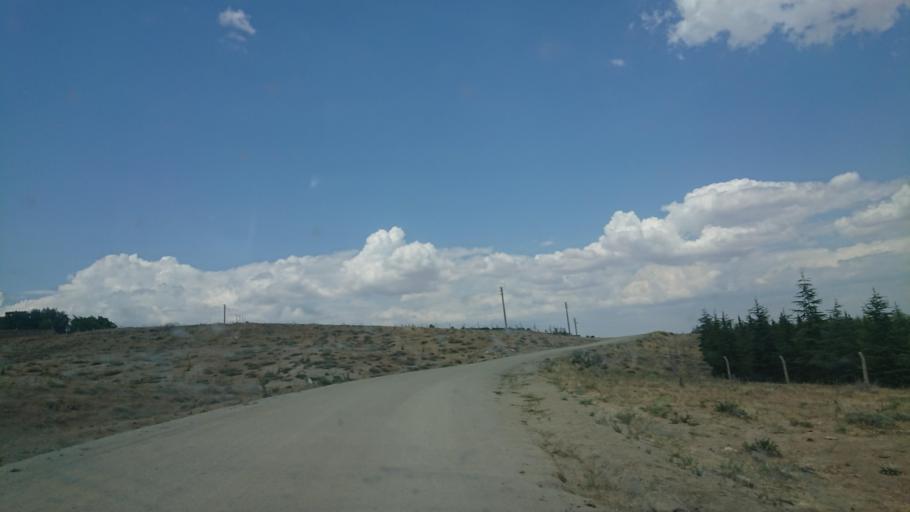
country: TR
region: Aksaray
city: Sariyahsi
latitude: 38.9493
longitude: 33.8809
